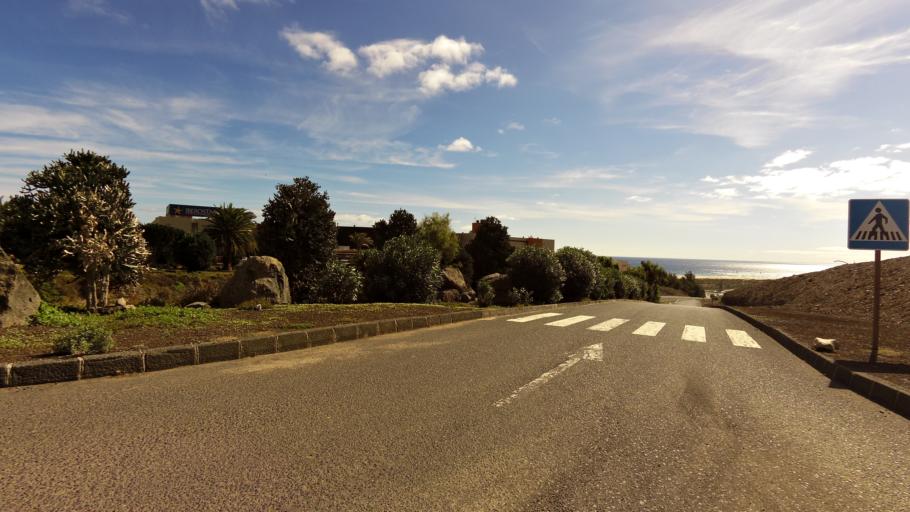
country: ES
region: Canary Islands
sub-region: Provincia de Las Palmas
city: Pajara
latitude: 28.0593
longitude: -14.3208
